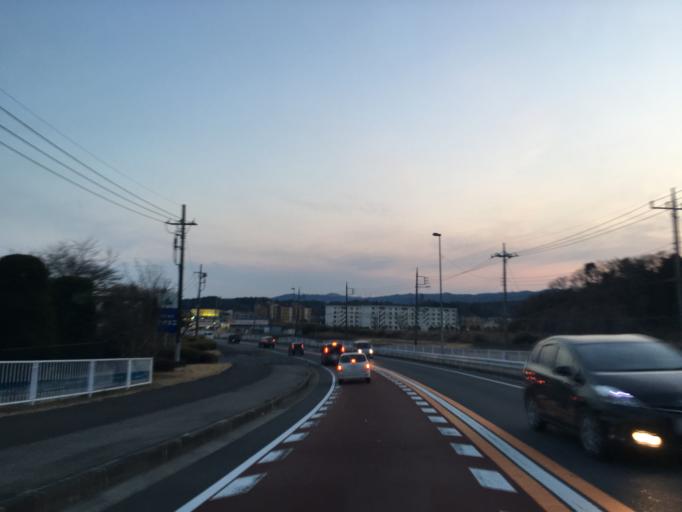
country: JP
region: Ibaraki
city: Takahagi
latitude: 36.7336
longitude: 140.7211
